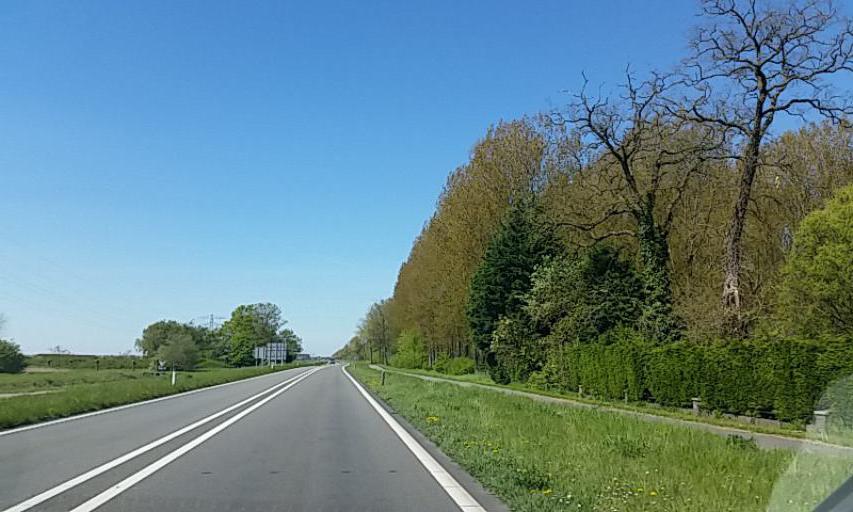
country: NL
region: Zeeland
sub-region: Gemeente Terneuzen
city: Axel
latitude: 51.2530
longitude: 3.9117
